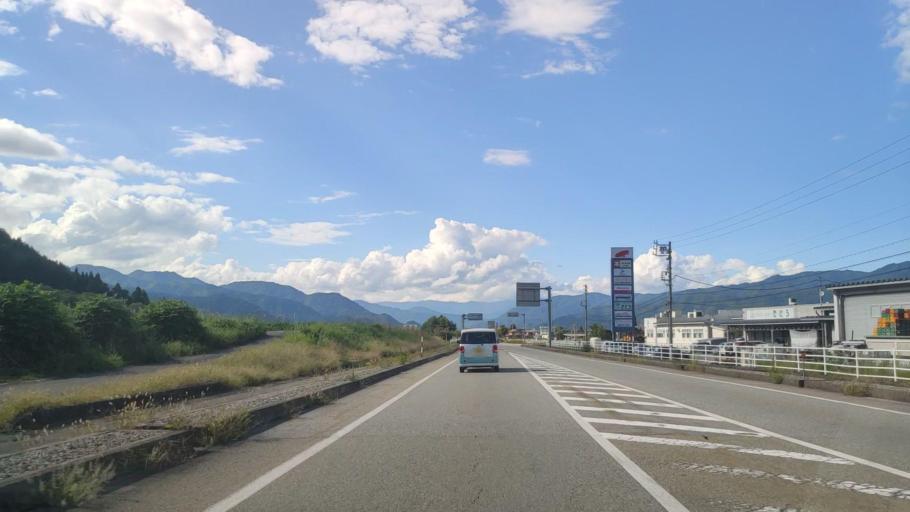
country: JP
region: Gifu
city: Takayama
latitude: 36.2126
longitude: 137.2076
